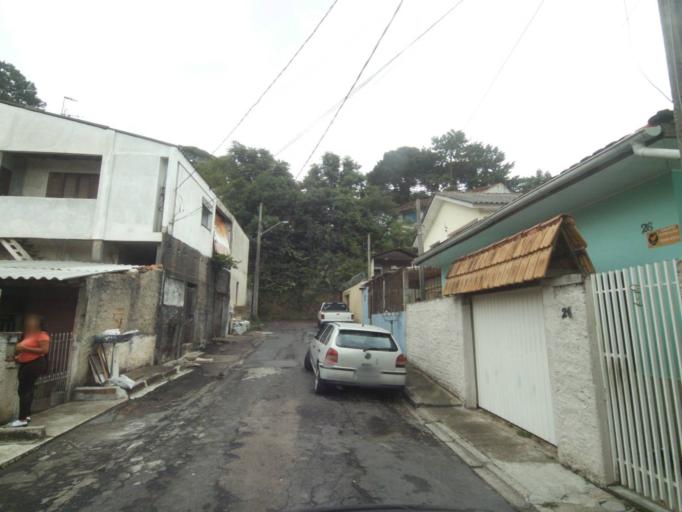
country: BR
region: Parana
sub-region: Curitiba
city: Curitiba
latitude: -25.4715
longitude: -49.3261
